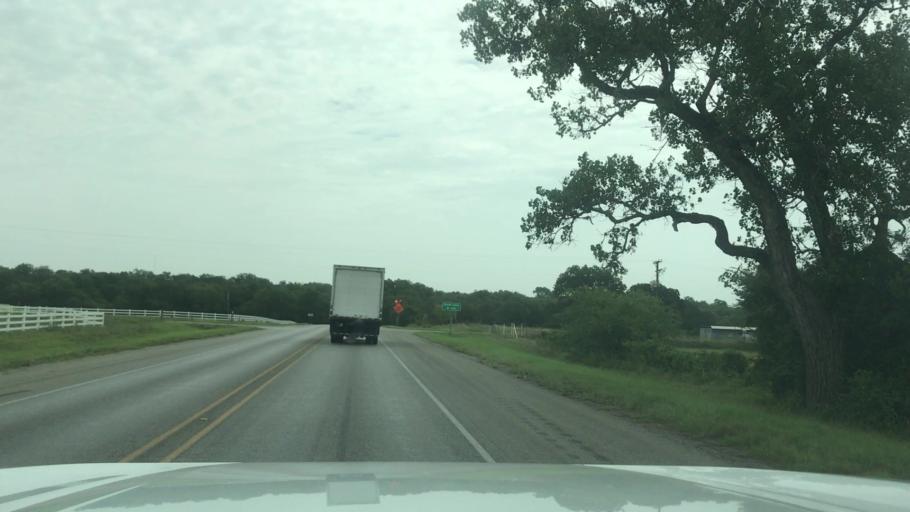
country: US
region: Texas
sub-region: Comanche County
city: De Leon
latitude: 32.1042
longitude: -98.4856
